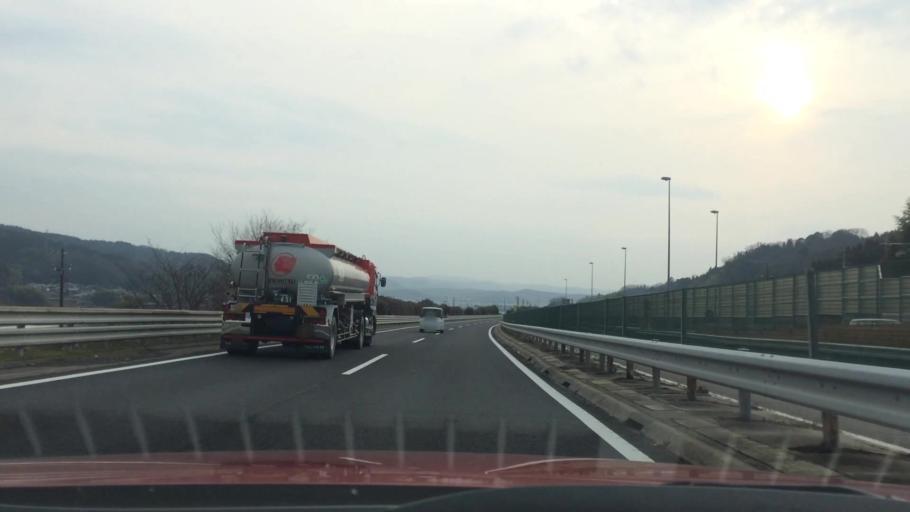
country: JP
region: Gifu
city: Mizunami
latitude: 35.3951
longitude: 137.2755
